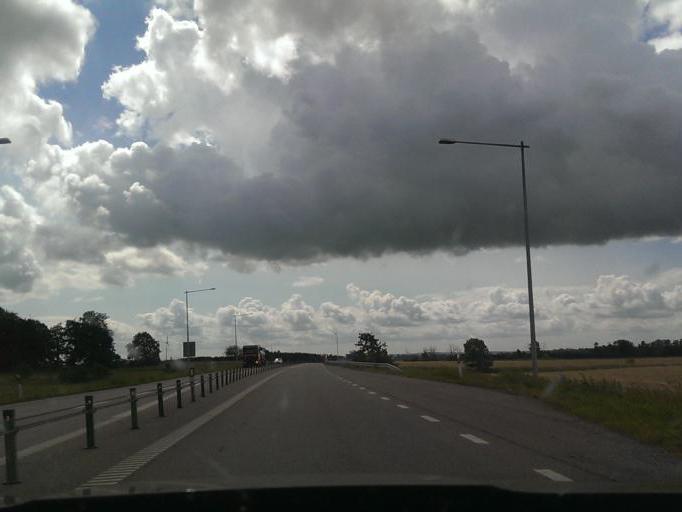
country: SE
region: Skane
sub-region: Eslovs Kommun
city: Eslov
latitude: 55.8267
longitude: 13.3341
